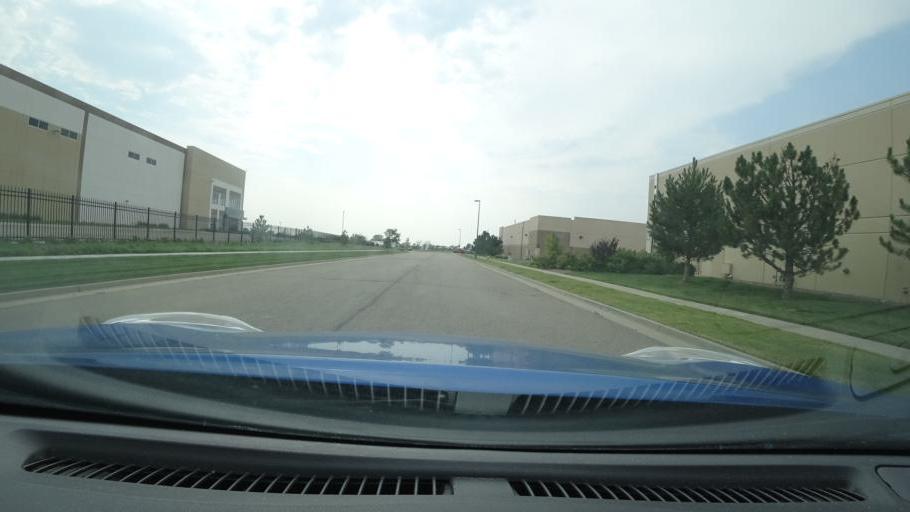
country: US
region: Colorado
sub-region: Adams County
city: Aurora
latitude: 39.7518
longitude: -104.7593
